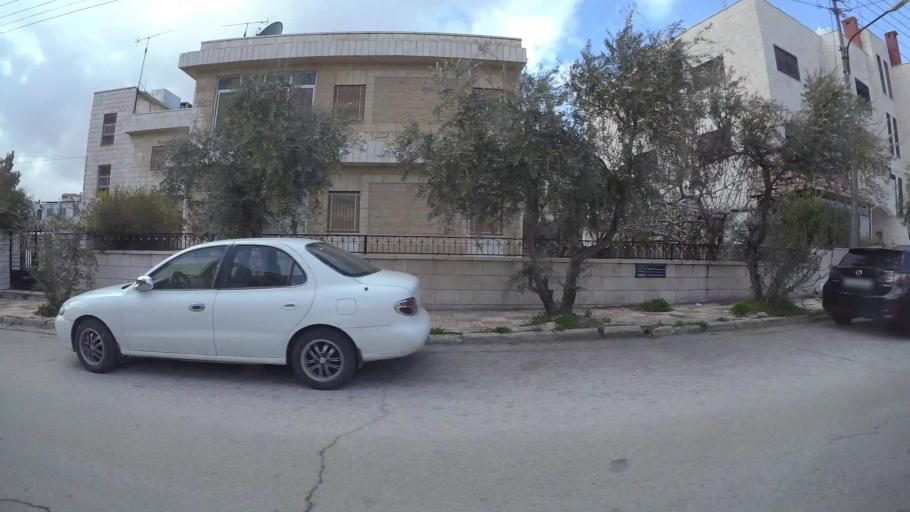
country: JO
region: Amman
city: Al Jubayhah
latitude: 31.9806
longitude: 35.8586
